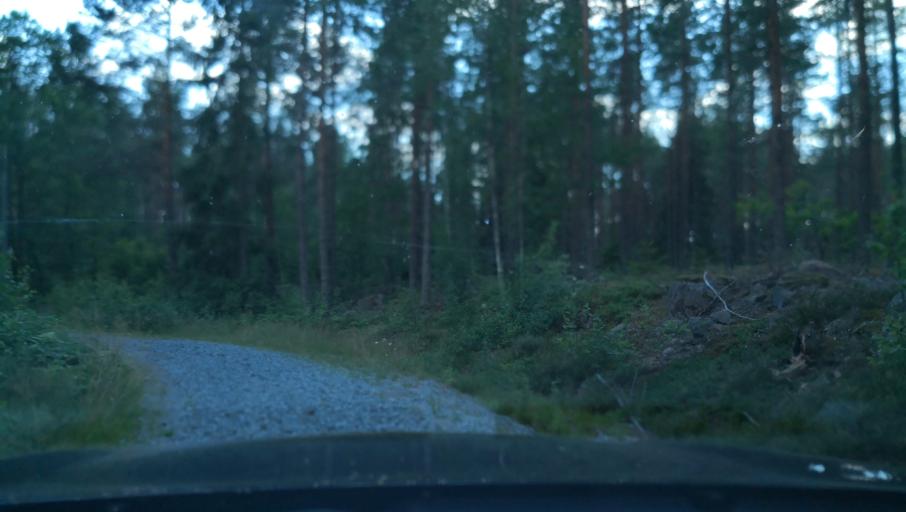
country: SE
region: Vaestmanland
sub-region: Vasteras
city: Skultuna
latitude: 59.7249
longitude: 16.3851
